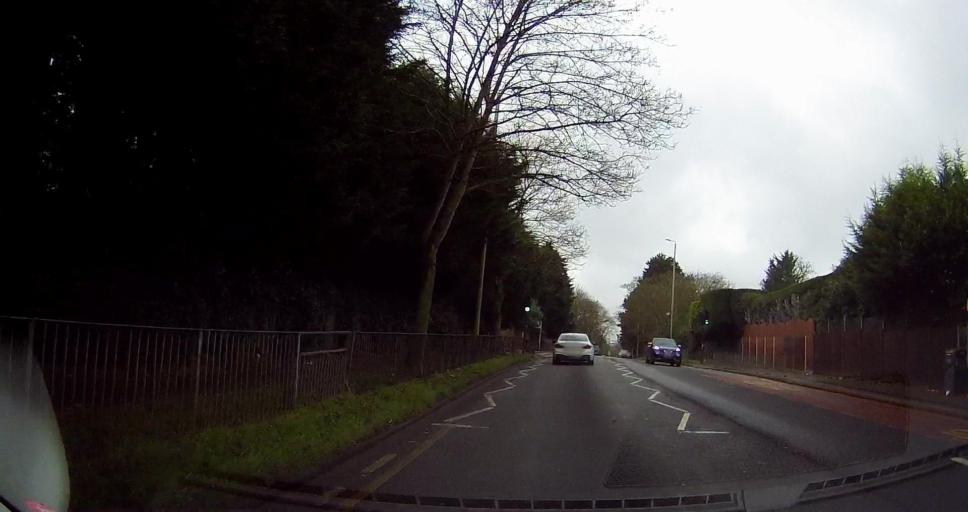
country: GB
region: England
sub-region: Greater London
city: Sidcup
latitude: 51.4167
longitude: 0.0905
